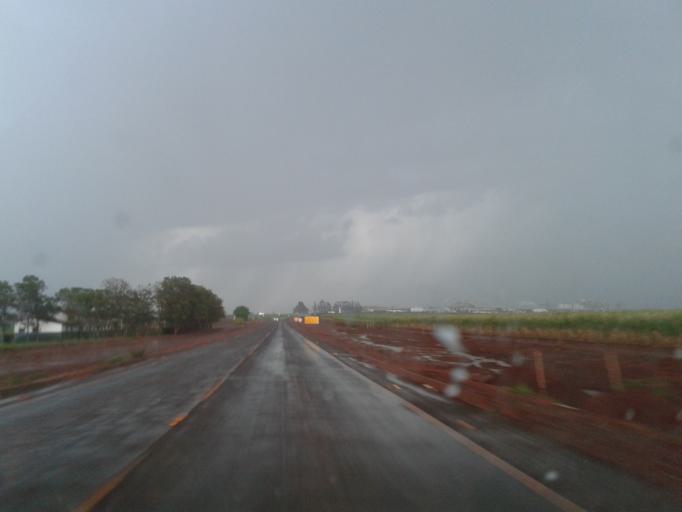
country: BR
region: Goias
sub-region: Quirinopolis
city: Quirinopolis
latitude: -18.5626
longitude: -50.4388
